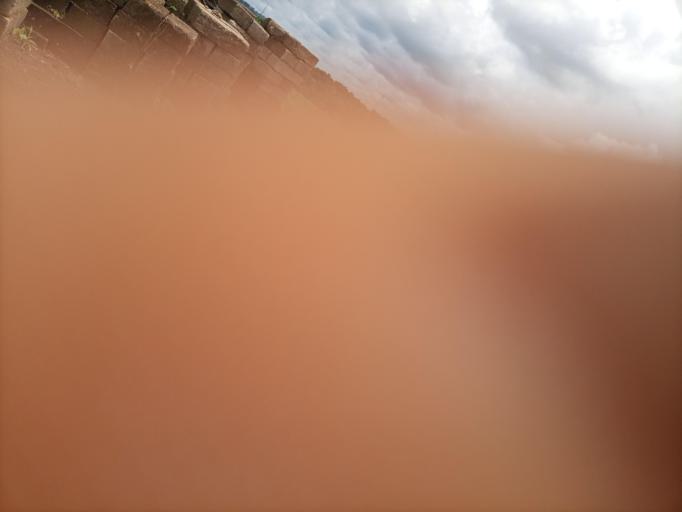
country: SL
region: Southern Province
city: Baoma
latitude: 7.9777
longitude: -11.7203
